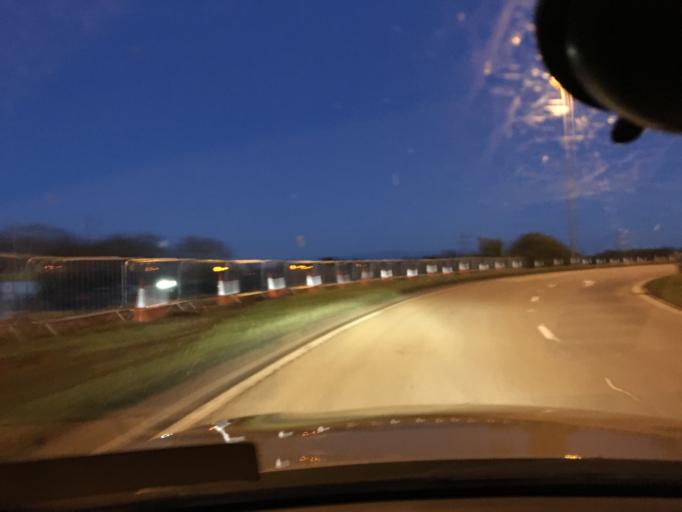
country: GB
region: Northern Ireland
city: Hillsborough
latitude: 54.4952
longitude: -6.0617
